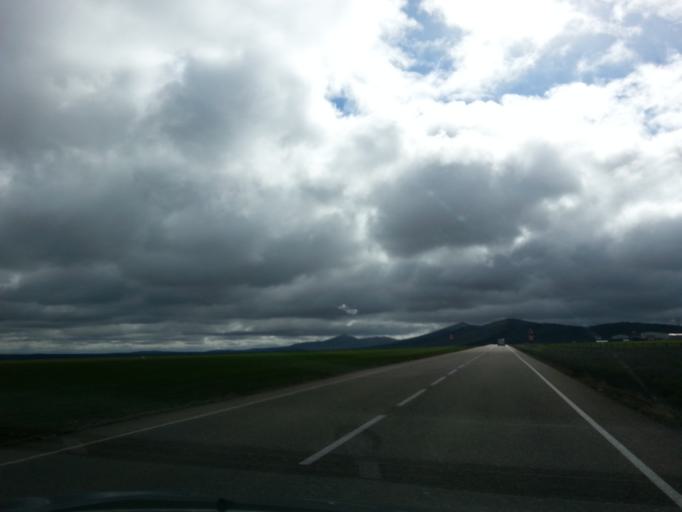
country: ES
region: Castille and Leon
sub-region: Provincia de Salamanca
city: Tamames
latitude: 40.6684
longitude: -6.1177
